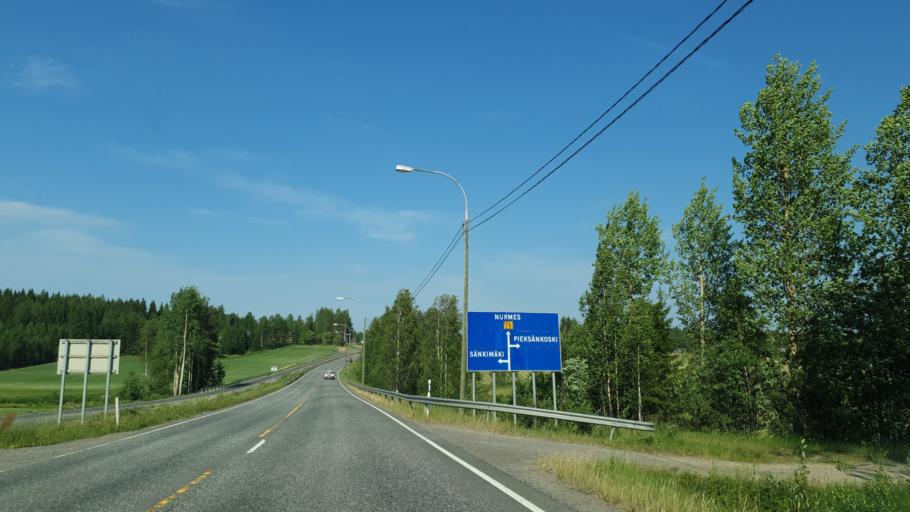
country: FI
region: Northern Savo
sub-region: Kuopio
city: Siilinjaervi
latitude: 63.1393
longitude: 27.8512
